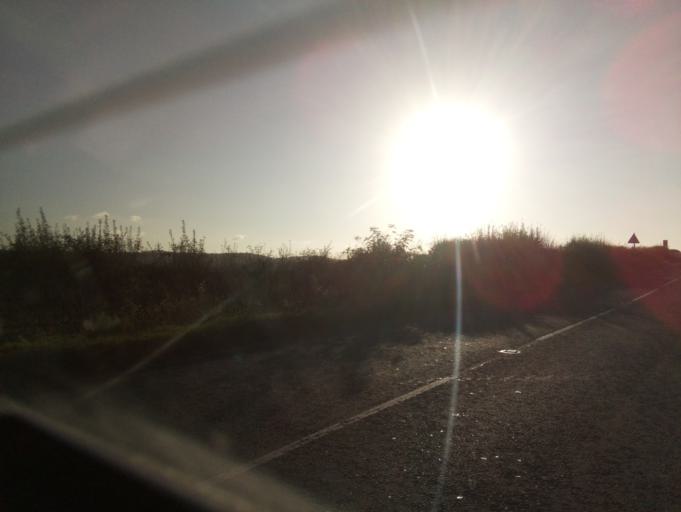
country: GB
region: England
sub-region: Somerset
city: Milborne Port
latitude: 50.9619
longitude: -2.4867
